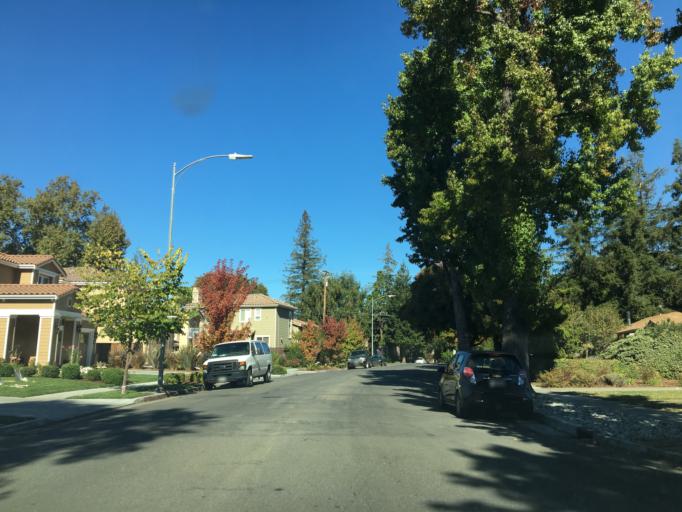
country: US
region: California
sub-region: Santa Clara County
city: San Jose
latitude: 37.3029
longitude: -121.8829
